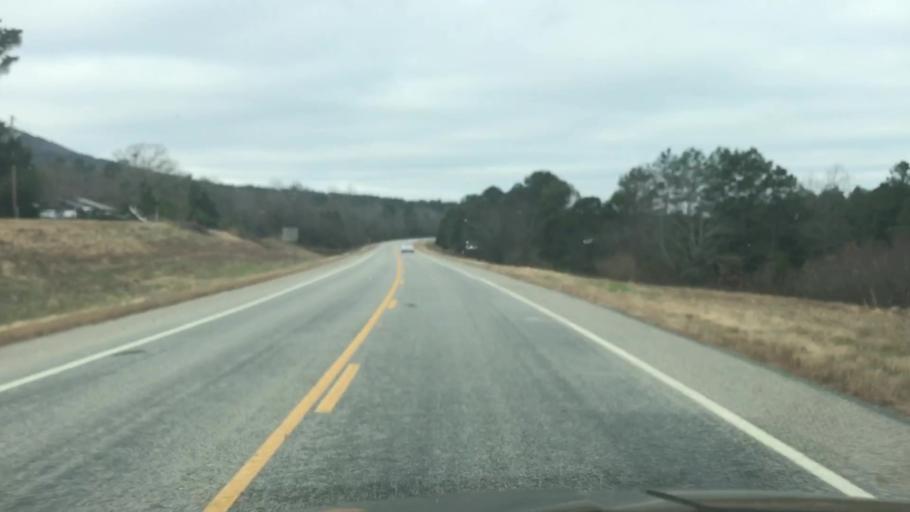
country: US
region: Arkansas
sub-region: Scott County
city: Waldron
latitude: 34.7034
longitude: -93.9223
